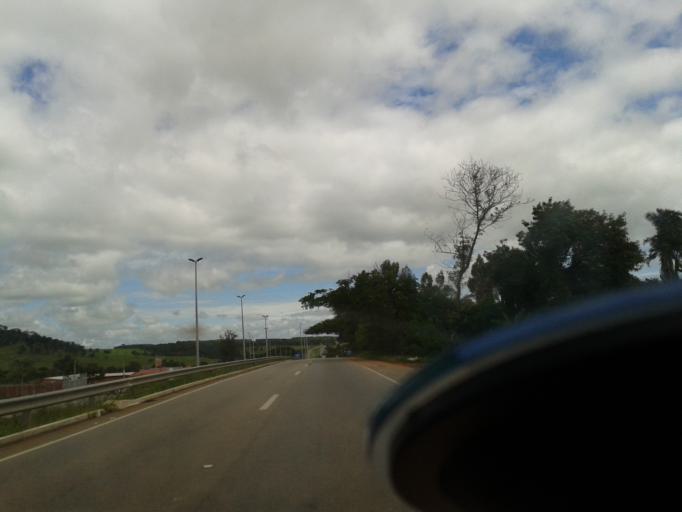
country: BR
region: Goias
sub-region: Inhumas
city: Inhumas
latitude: -16.3636
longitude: -49.5089
